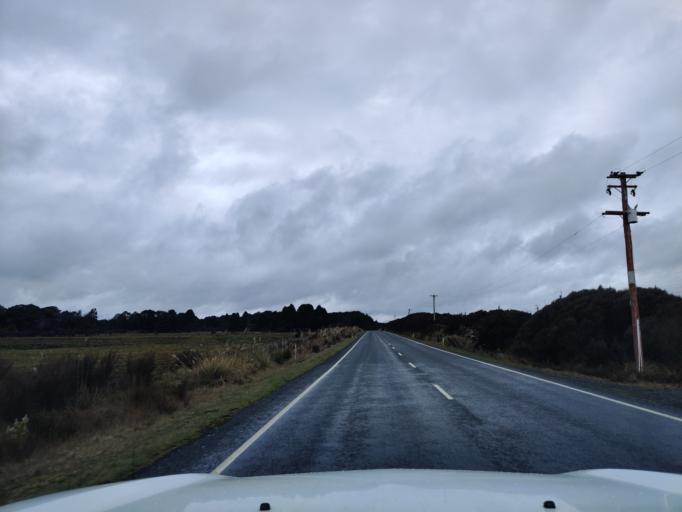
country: NZ
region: Manawatu-Wanganui
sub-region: Ruapehu District
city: Waiouru
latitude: -39.3390
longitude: 175.3788
